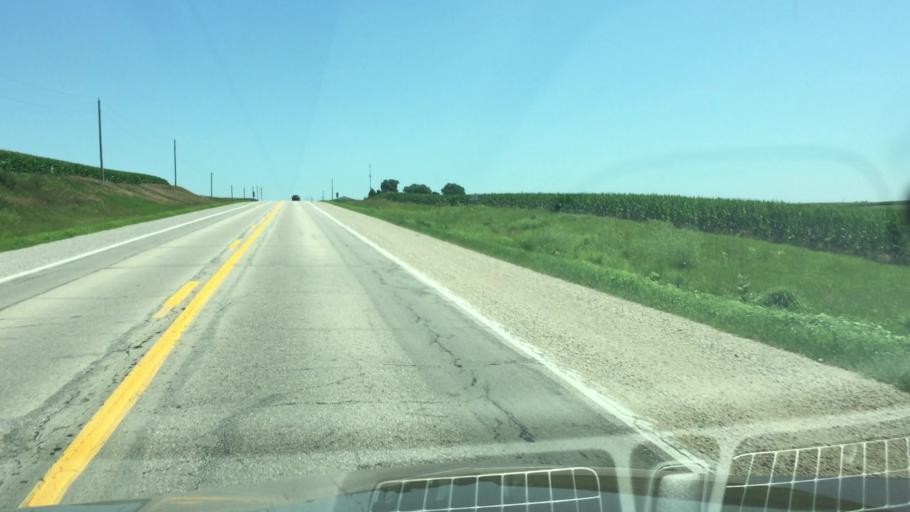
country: US
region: Iowa
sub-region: Cedar County
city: Mechanicsville
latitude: 41.8887
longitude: -91.1988
